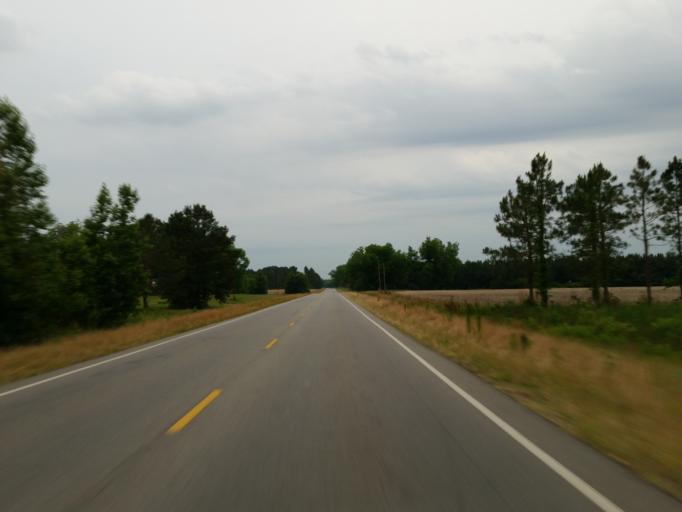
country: US
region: Georgia
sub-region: Dooly County
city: Vienna
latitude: 32.0601
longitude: -83.7978
